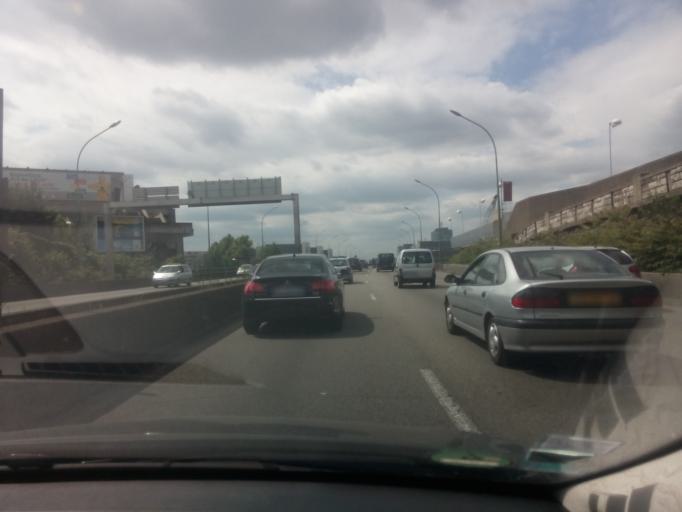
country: FR
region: Ile-de-France
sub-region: Departement des Hauts-de-Seine
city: Vanves
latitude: 48.8280
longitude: 2.2917
